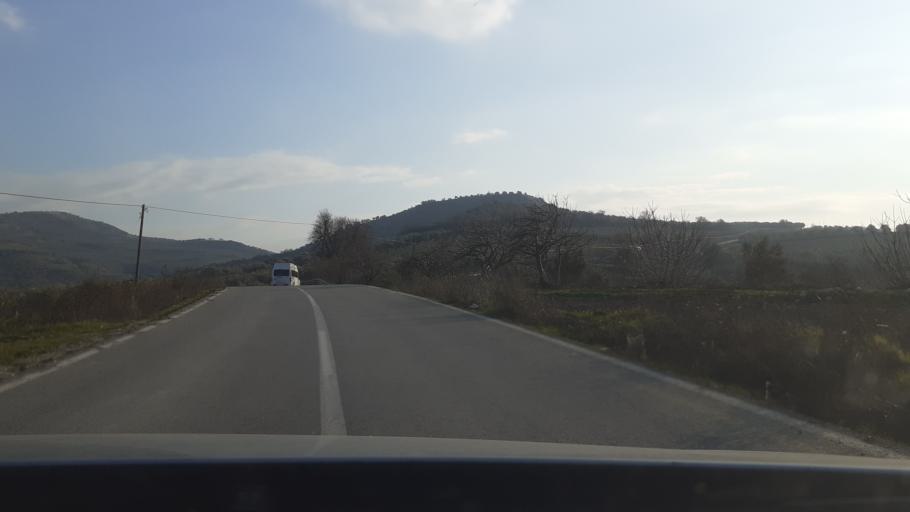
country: TR
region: Hatay
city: Oymakli
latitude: 36.1265
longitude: 36.3097
